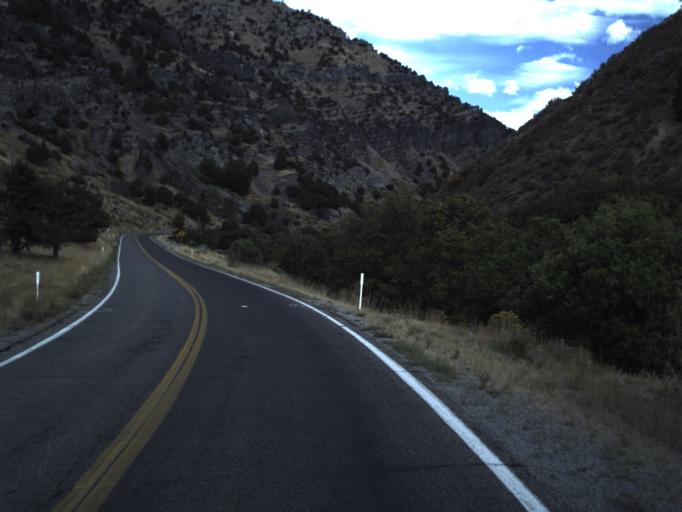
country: US
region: Utah
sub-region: Cache County
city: Hyrum
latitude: 41.6250
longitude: -111.7945
